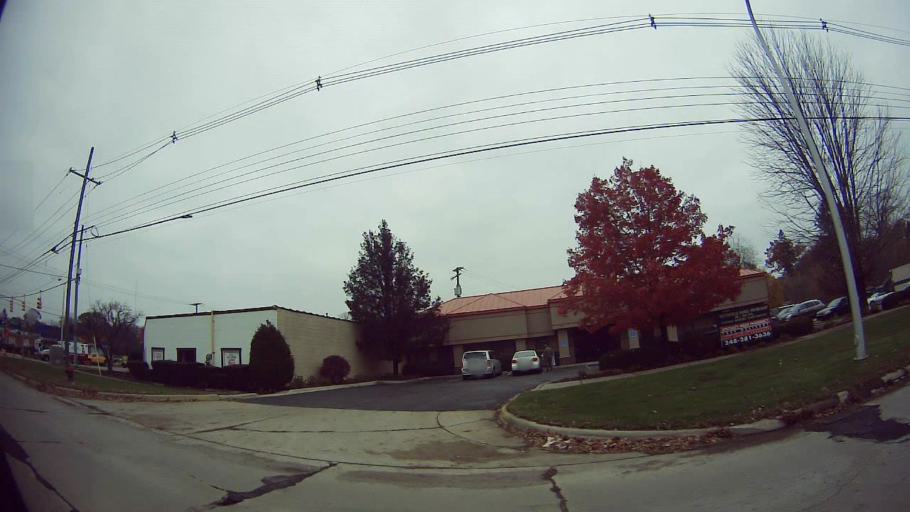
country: US
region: Michigan
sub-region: Oakland County
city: Southfield
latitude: 42.4567
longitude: -83.2599
